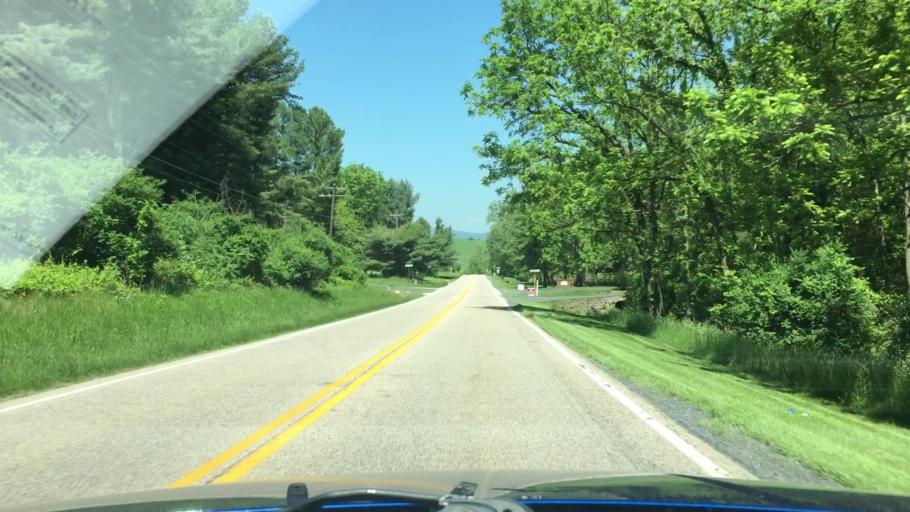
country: US
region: Virginia
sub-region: City of Staunton
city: Staunton
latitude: 38.1893
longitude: -79.1058
